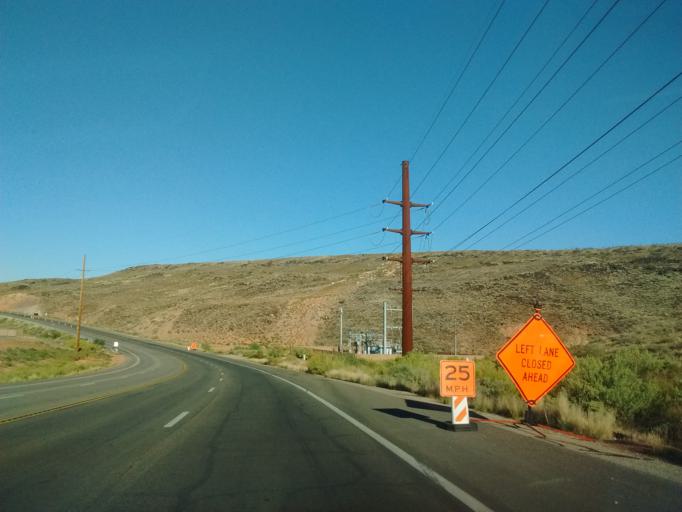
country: US
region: Utah
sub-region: Washington County
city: Washington
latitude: 37.1315
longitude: -113.4834
